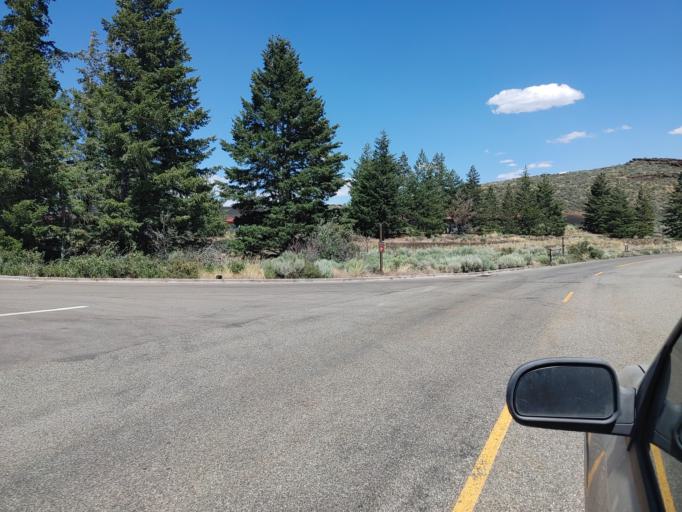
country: US
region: Idaho
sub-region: Butte County
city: Arco
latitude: 43.4618
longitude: -113.5606
